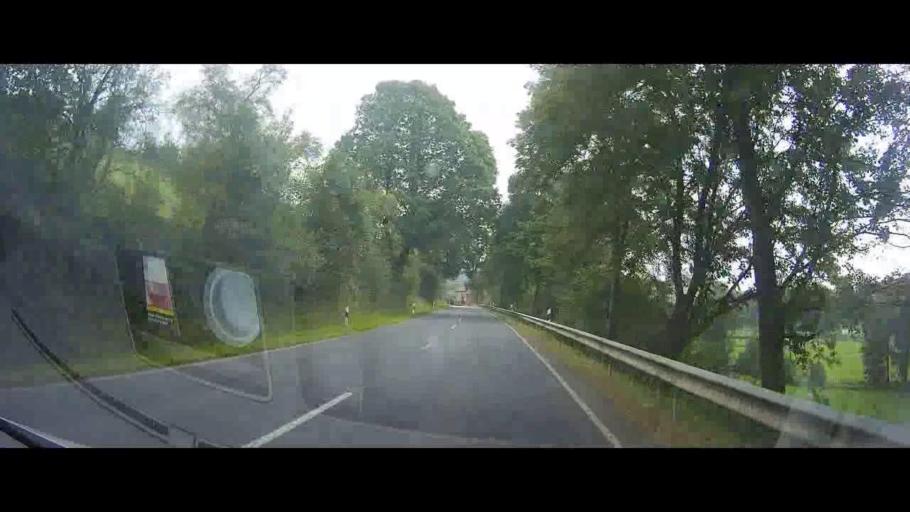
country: DE
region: Lower Saxony
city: Uslar
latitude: 51.5977
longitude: 9.6752
